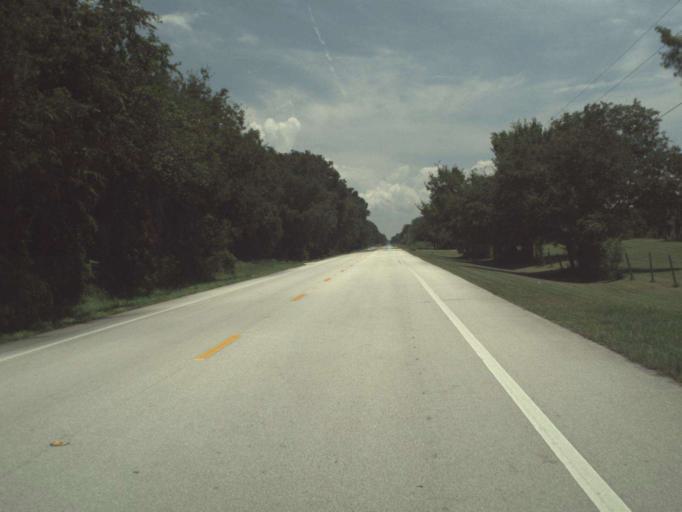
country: US
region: Florida
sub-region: Martin County
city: Indiantown
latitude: 27.0457
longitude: -80.6408
